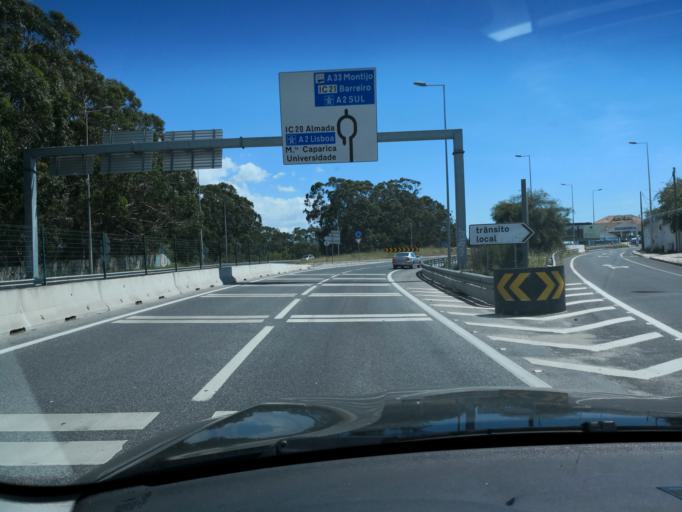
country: PT
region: Setubal
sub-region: Almada
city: Caparica
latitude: 38.6557
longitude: -9.2010
